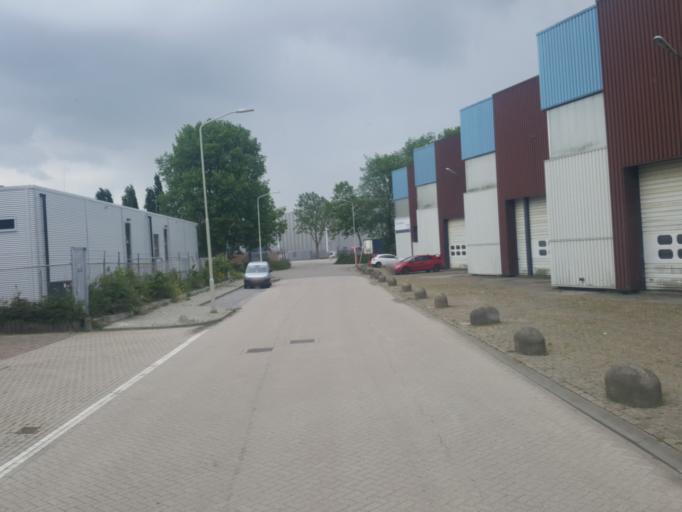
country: NL
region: South Holland
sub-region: Gemeente Gorinchem
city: Gorinchem
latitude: 51.8318
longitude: 4.9503
